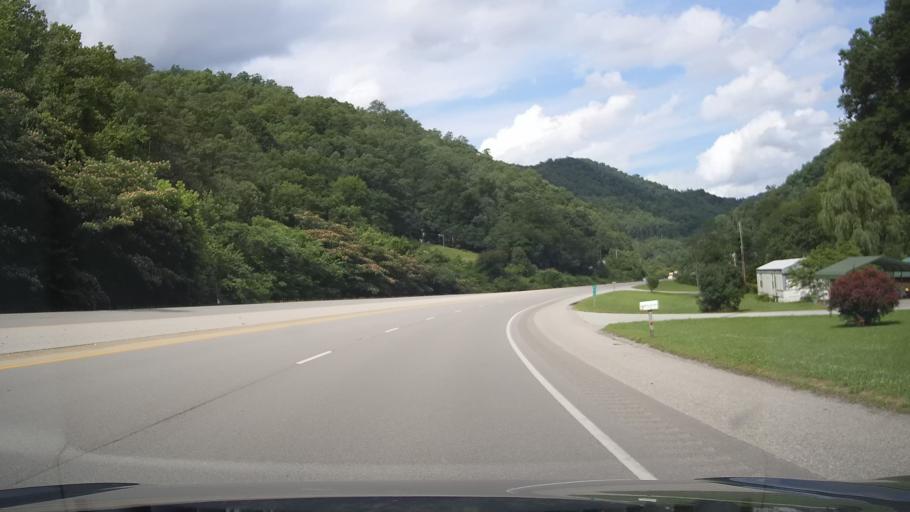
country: US
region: Kentucky
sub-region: Pike County
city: Pikeville
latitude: 37.3401
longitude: -82.5553
